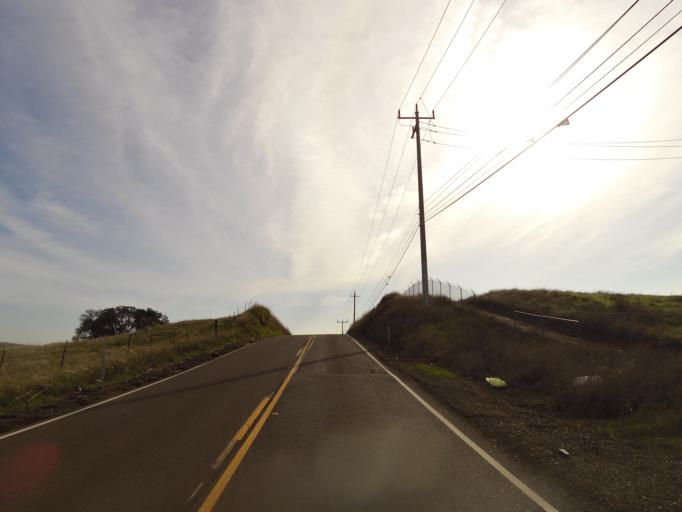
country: US
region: California
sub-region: Sacramento County
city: Folsom
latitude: 38.6292
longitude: -121.1504
